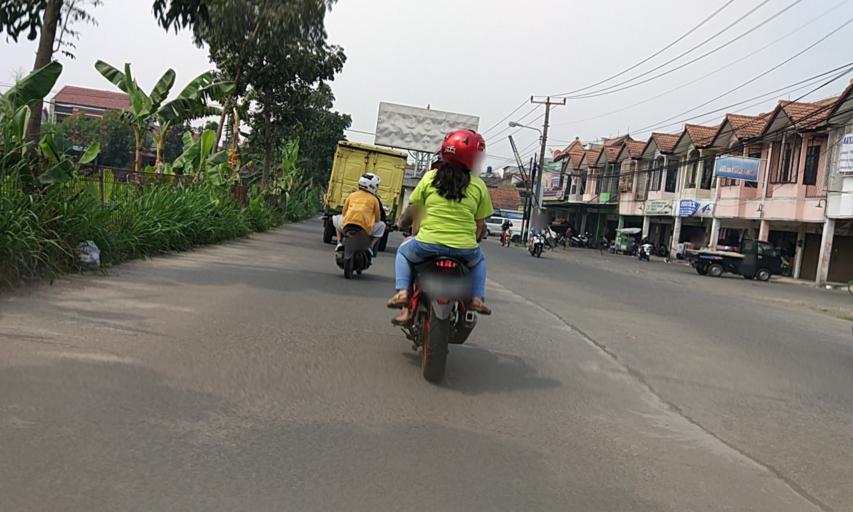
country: ID
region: West Java
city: Margahayukencana
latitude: -6.9411
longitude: 107.5654
